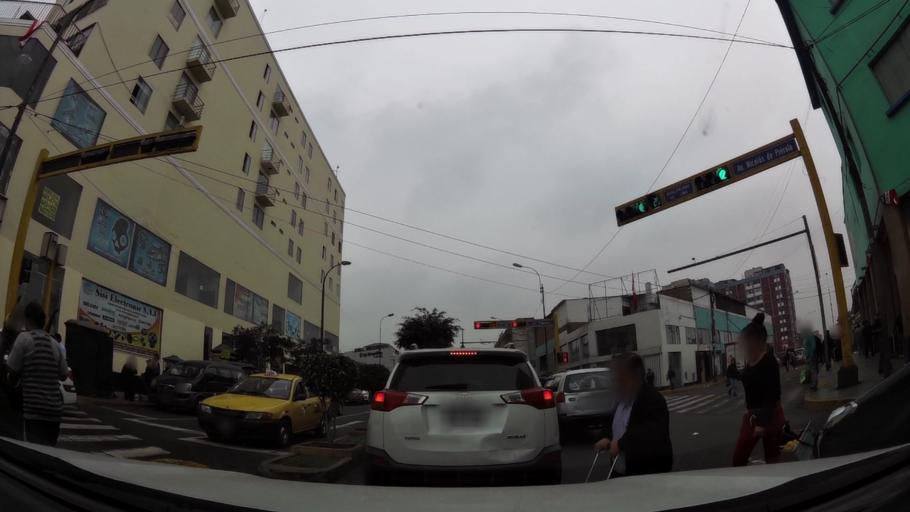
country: PE
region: Lima
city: Lima
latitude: -12.0575
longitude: -77.0257
